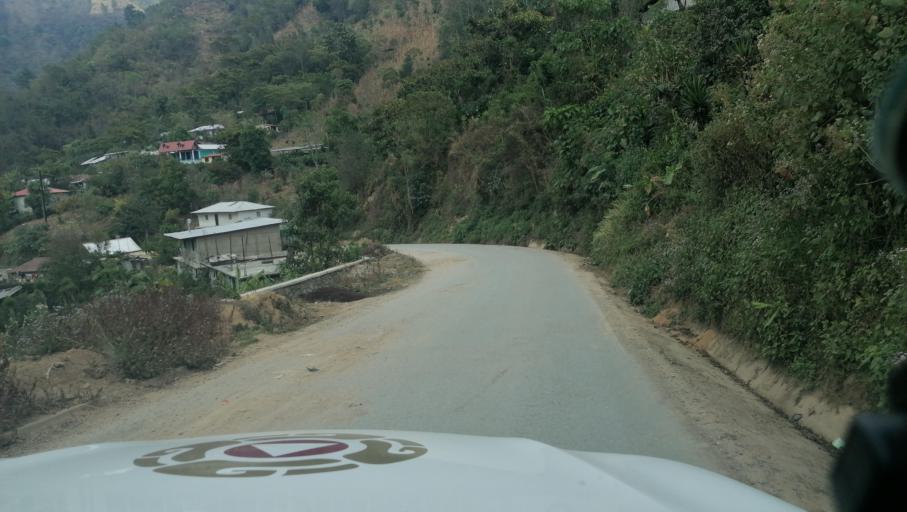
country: GT
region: San Marcos
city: Tacana
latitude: 15.2070
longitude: -92.1940
